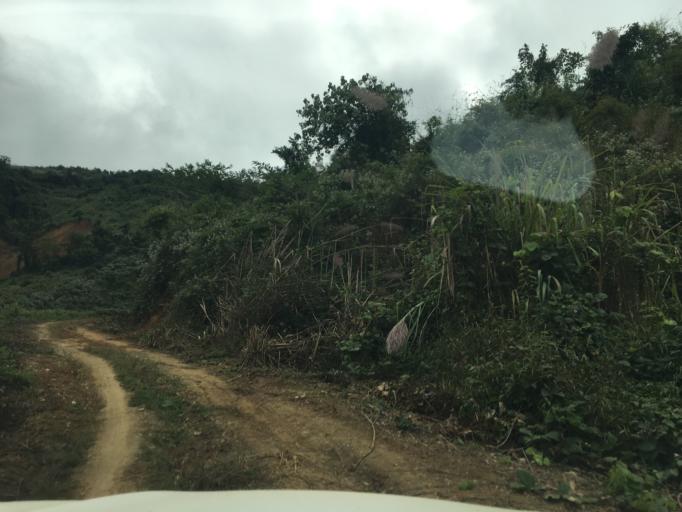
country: LA
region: Houaphan
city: Viengthong
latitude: 19.9368
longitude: 103.2946
